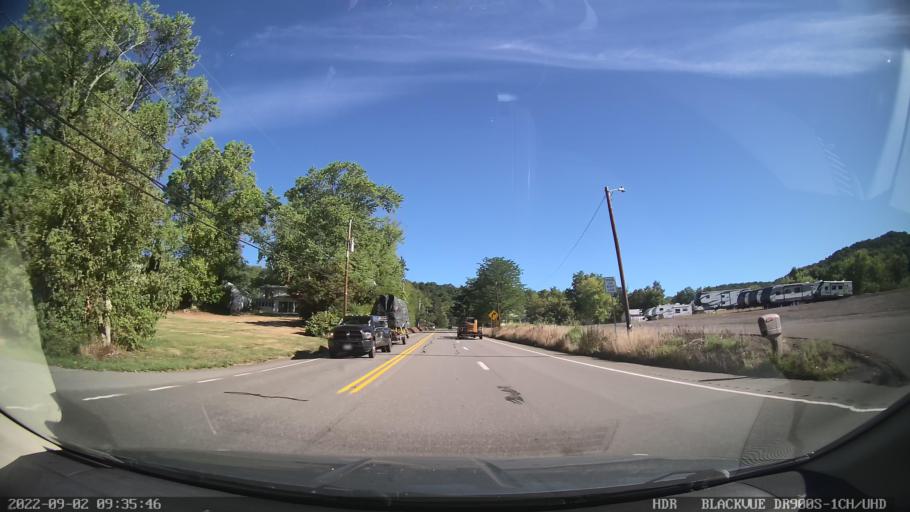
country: US
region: Pennsylvania
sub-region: Northumberland County
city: Elysburg
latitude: 40.8755
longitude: -76.5552
